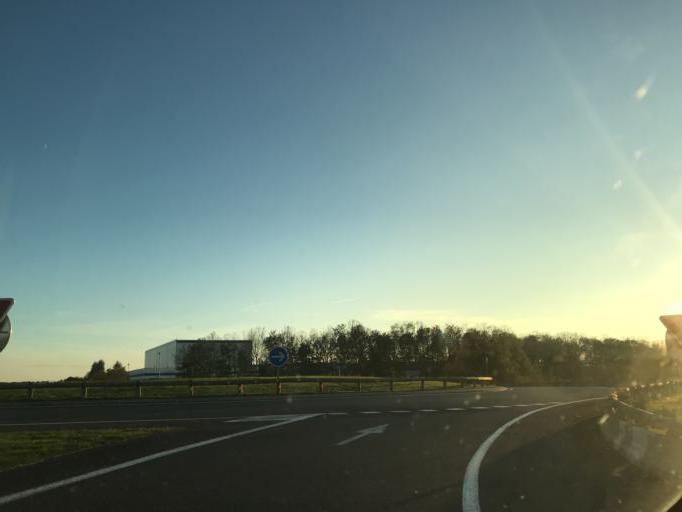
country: FR
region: Bourgogne
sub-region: Departement de l'Yonne
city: Egriselles-le-Bocage
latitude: 48.1665
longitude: 3.1755
